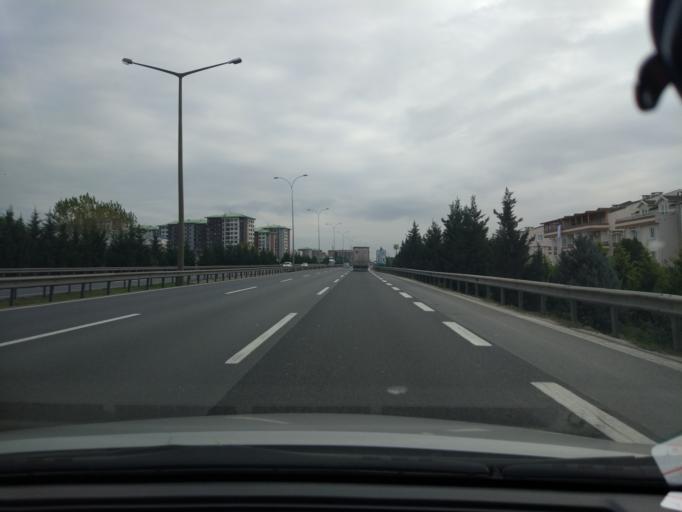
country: TR
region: Kocaeli
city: Korfez
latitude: 40.7703
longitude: 29.7901
